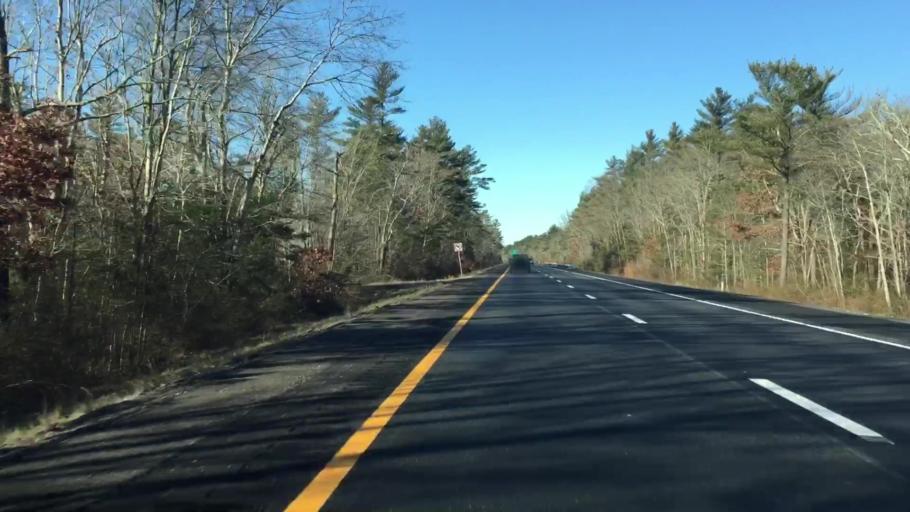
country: US
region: Massachusetts
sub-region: Plymouth County
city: West Wareham
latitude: 41.8330
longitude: -70.8185
